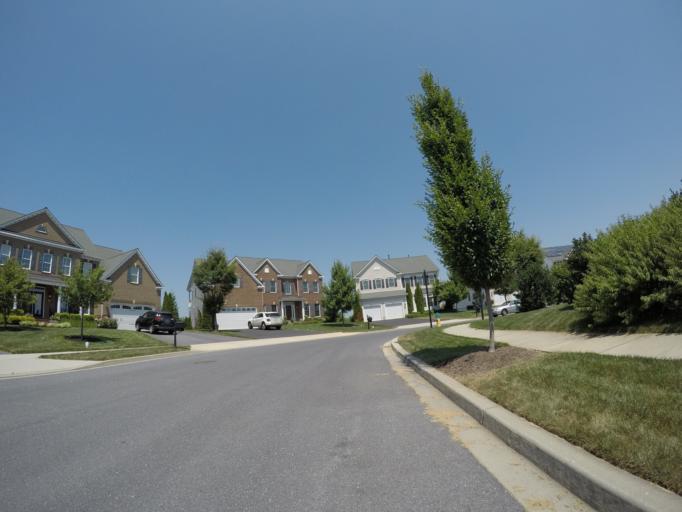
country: US
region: Maryland
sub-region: Frederick County
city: Urbana
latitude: 39.3374
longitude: -77.3595
